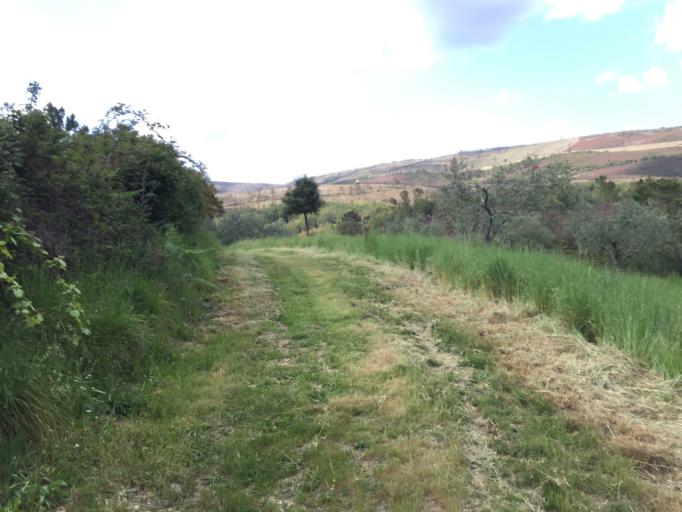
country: PT
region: Coimbra
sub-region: Pampilhosa da Serra
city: Pampilhosa da Serra
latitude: 40.1123
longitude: -7.8662
